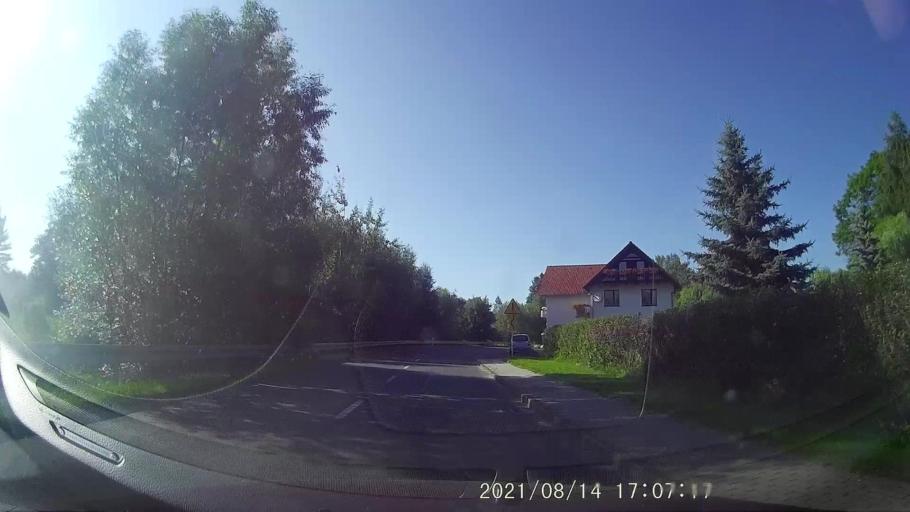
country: PL
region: Lower Silesian Voivodeship
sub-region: Powiat jeleniogorski
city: Kowary
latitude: 50.8161
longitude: 15.8092
